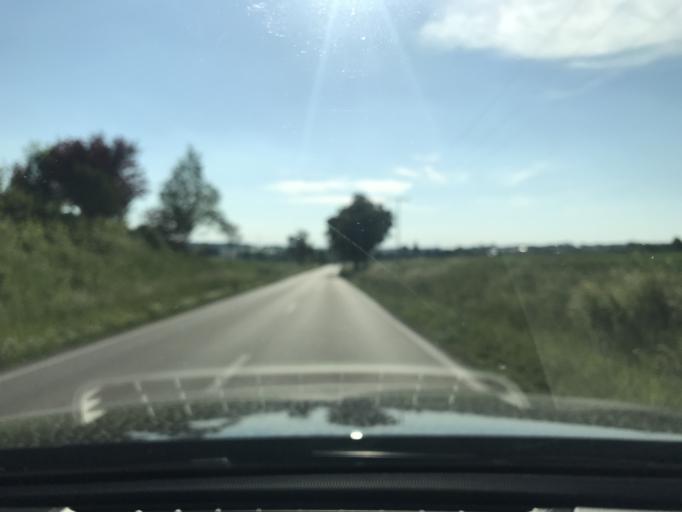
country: DE
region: Baden-Wuerttemberg
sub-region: Regierungsbezirk Stuttgart
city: Schwaikheim
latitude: 48.8911
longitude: 9.3320
